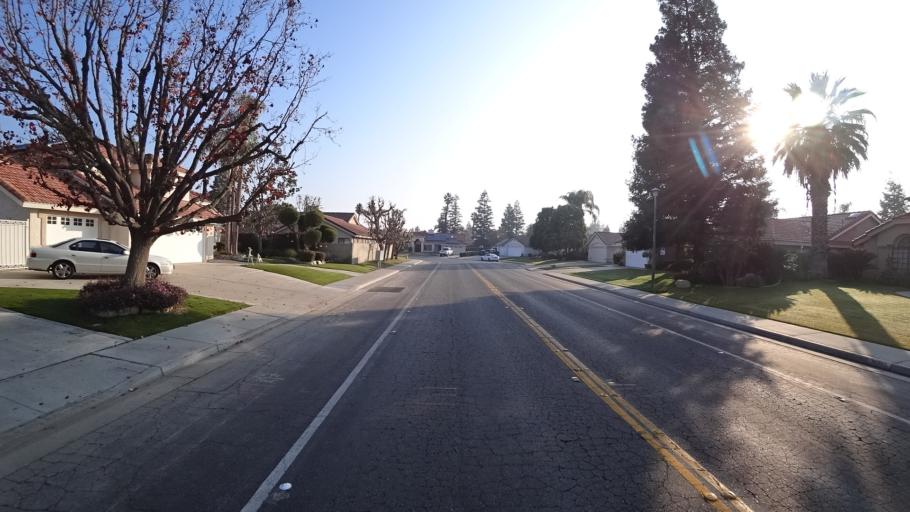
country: US
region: California
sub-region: Kern County
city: Greenacres
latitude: 35.3293
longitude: -119.1029
